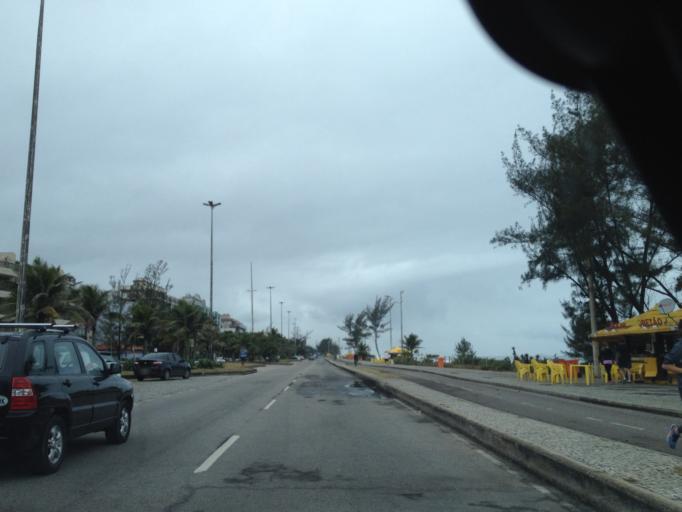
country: BR
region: Rio de Janeiro
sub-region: Nilopolis
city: Nilopolis
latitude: -23.0239
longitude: -43.4528
